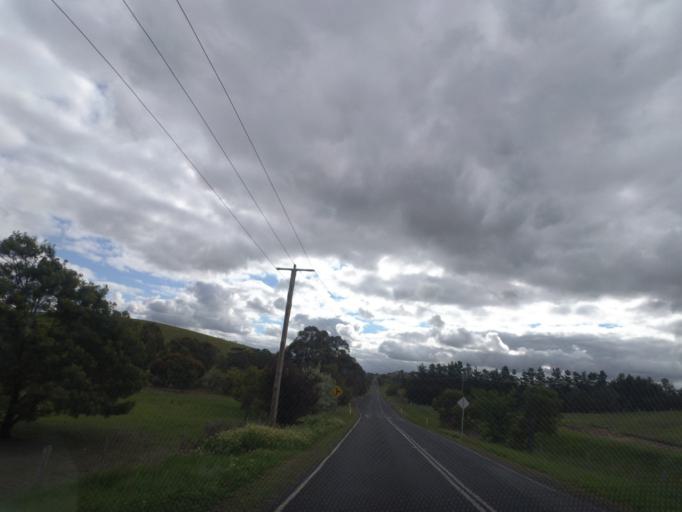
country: AU
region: Victoria
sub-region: Whittlesea
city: Whittlesea
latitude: -37.5211
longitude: 145.0435
